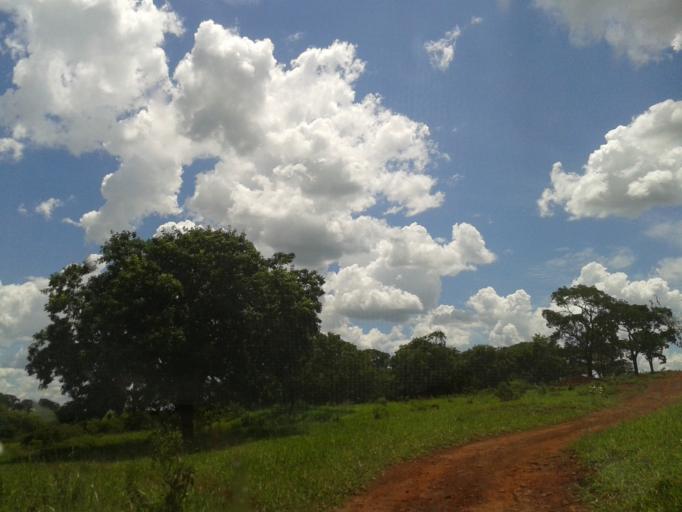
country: BR
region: Minas Gerais
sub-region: Capinopolis
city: Capinopolis
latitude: -18.7885
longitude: -49.8052
